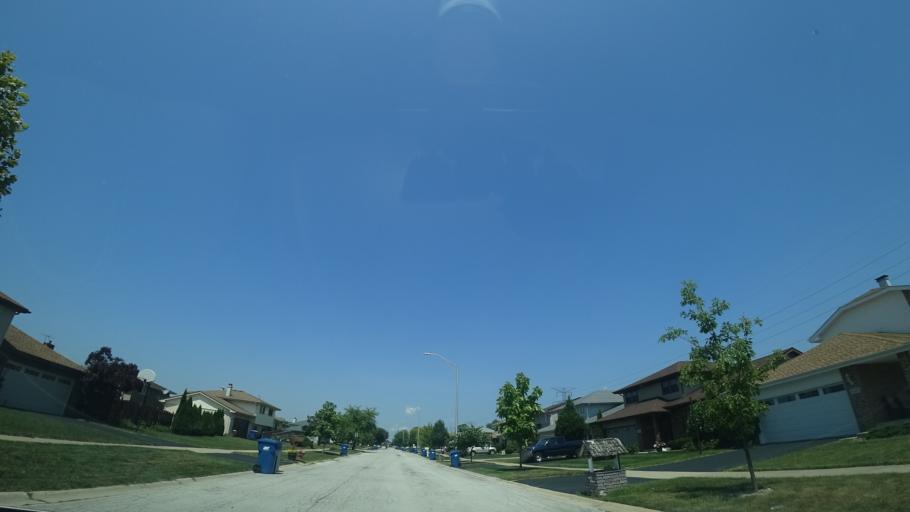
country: US
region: Illinois
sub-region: Cook County
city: Alsip
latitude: 41.6844
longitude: -87.7417
